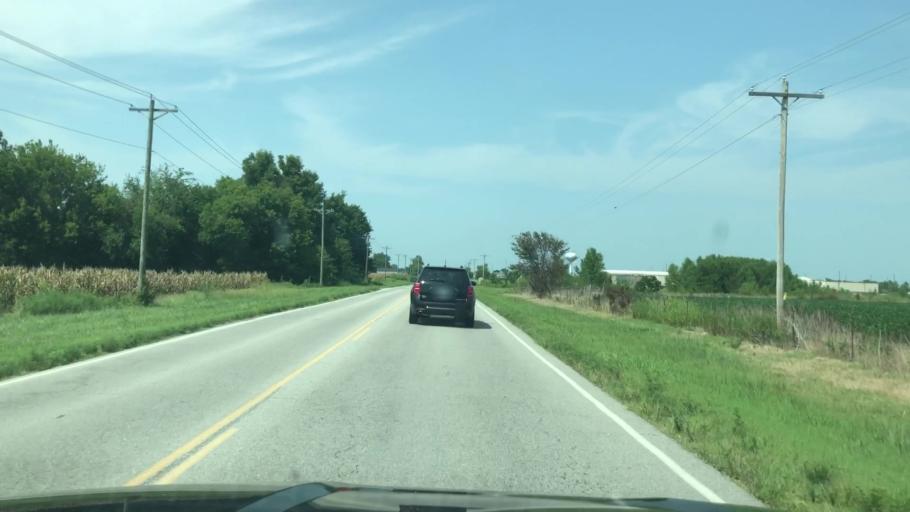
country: US
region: Oklahoma
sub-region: Ottawa County
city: Commerce
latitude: 36.9026
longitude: -94.8419
